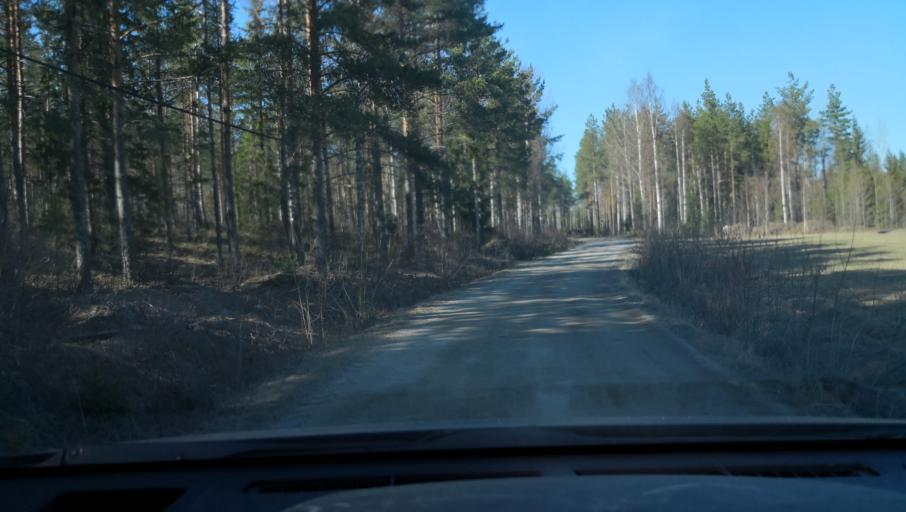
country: SE
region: Vaestmanland
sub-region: Sala Kommun
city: Sala
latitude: 59.9323
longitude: 16.4505
